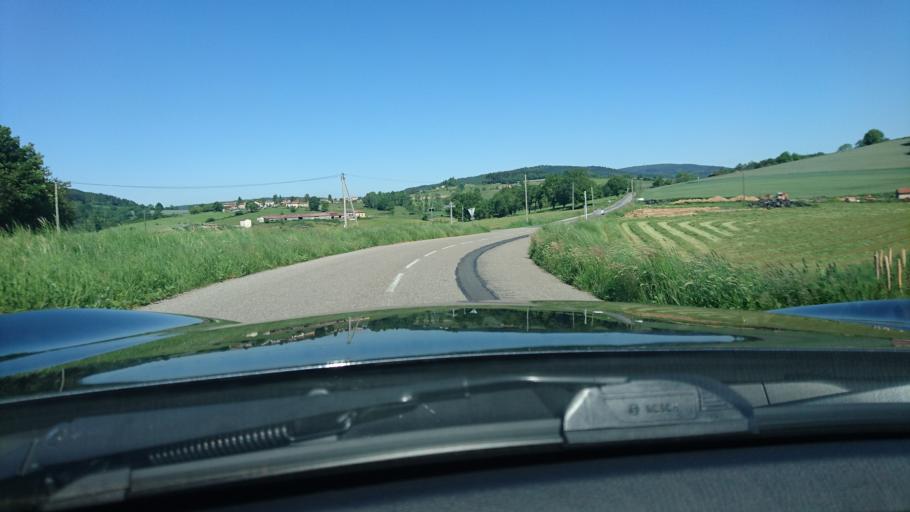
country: FR
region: Rhone-Alpes
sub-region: Departement du Rhone
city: Montrottier
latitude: 45.8044
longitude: 4.4267
